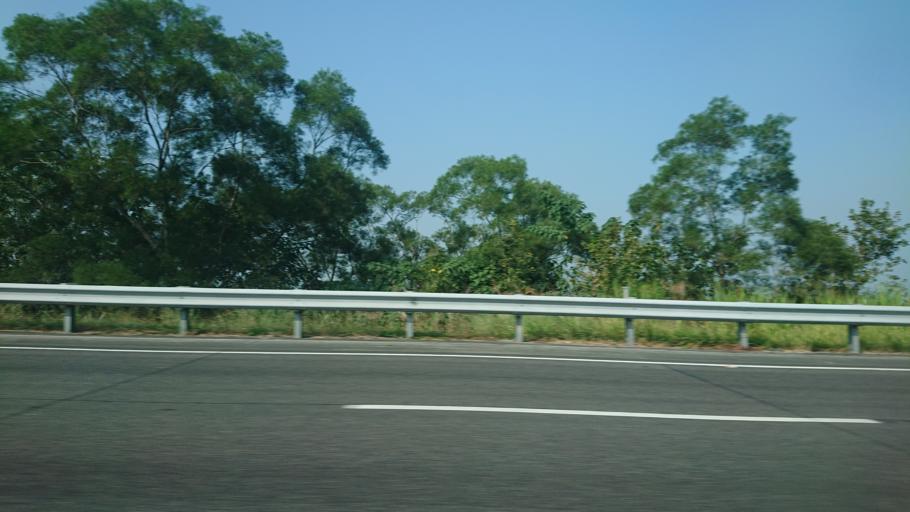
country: TW
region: Taiwan
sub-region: Nantou
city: Nantou
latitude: 23.8643
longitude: 120.7029
